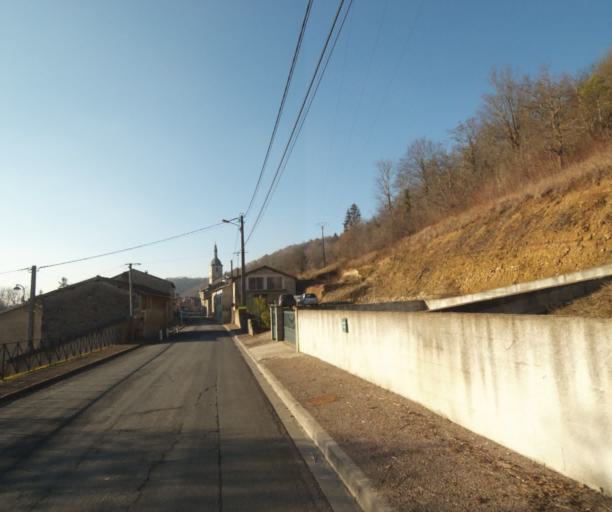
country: FR
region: Champagne-Ardenne
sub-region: Departement de la Haute-Marne
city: Chevillon
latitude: 48.5285
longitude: 5.1384
